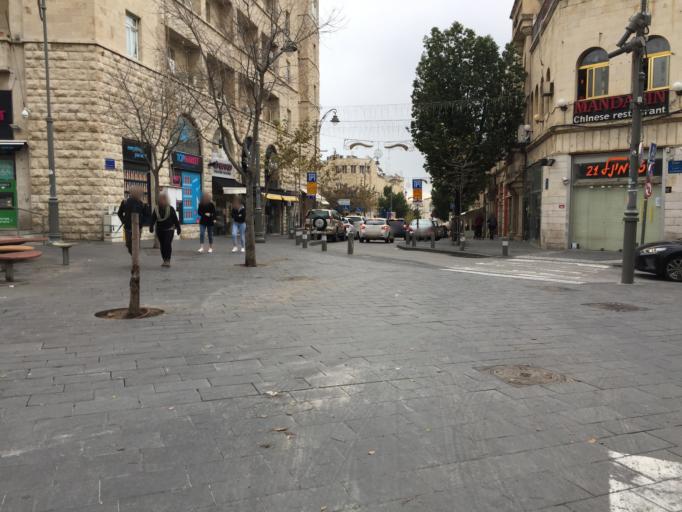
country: IL
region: Jerusalem
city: West Jerusalem
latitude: 31.7808
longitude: 35.2213
